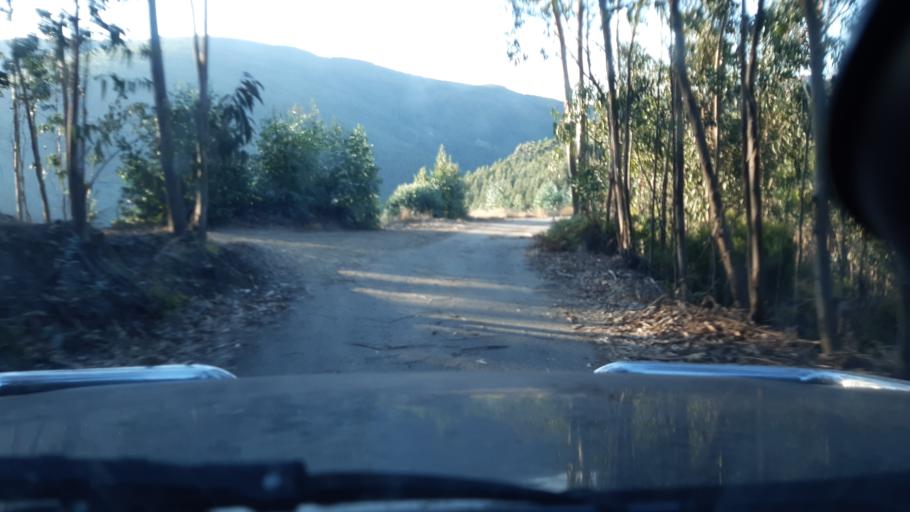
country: PT
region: Viseu
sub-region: Mortagua
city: Mortagua
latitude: 40.5237
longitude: -8.2536
